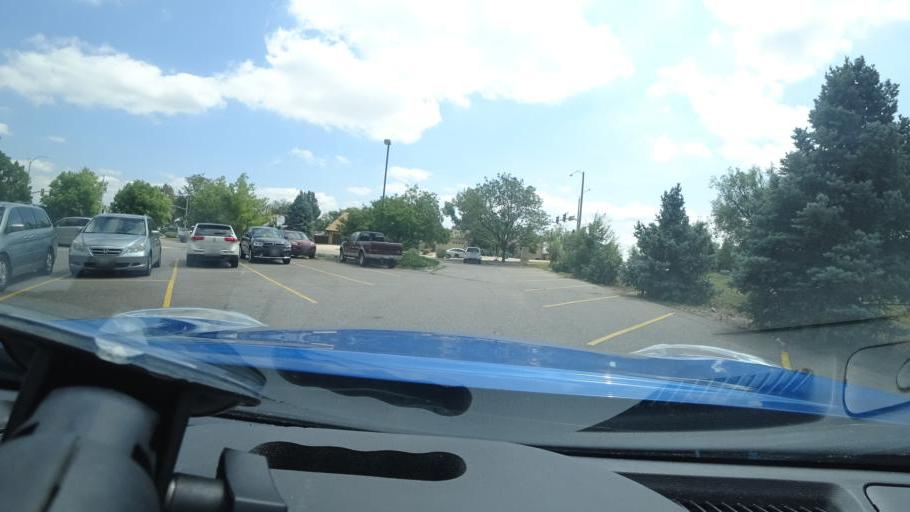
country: US
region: Colorado
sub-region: Adams County
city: Aurora
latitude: 39.7219
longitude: -104.8479
